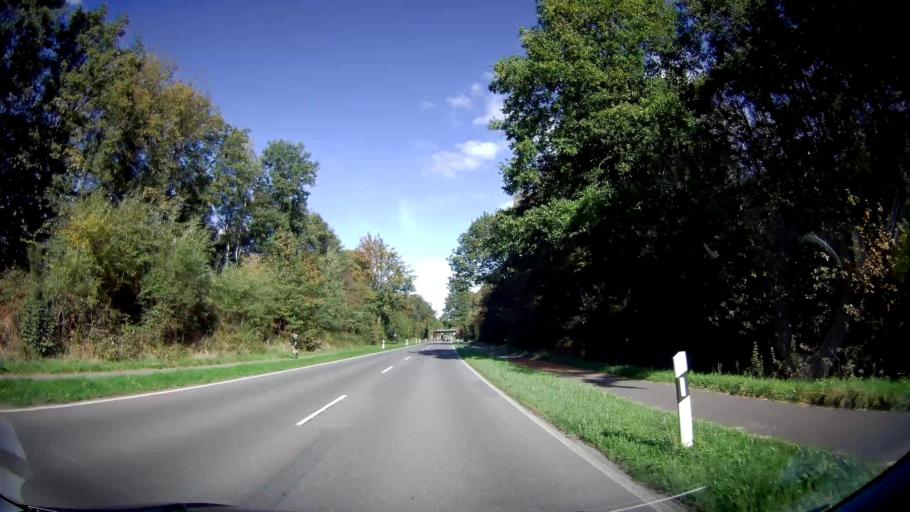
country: DE
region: North Rhine-Westphalia
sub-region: Regierungsbezirk Dusseldorf
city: Hunxe
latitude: 51.6222
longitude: 6.7552
